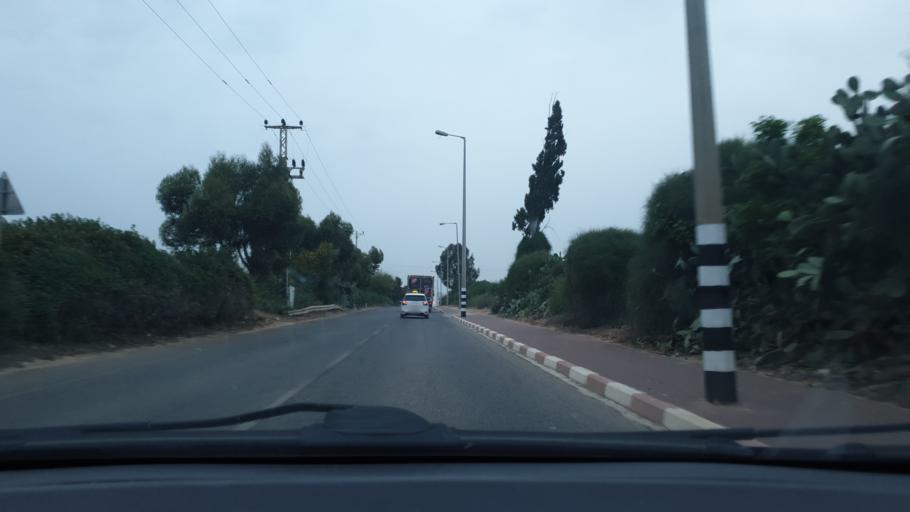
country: IL
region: Central District
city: Kefar Habad
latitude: 31.9809
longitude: 34.8388
